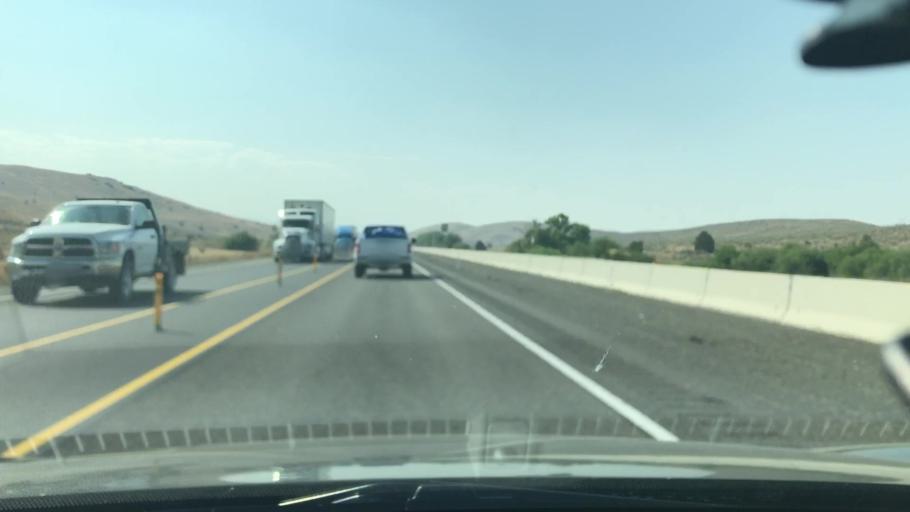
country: US
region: Oregon
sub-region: Baker County
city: Baker City
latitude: 44.6738
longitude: -117.6342
